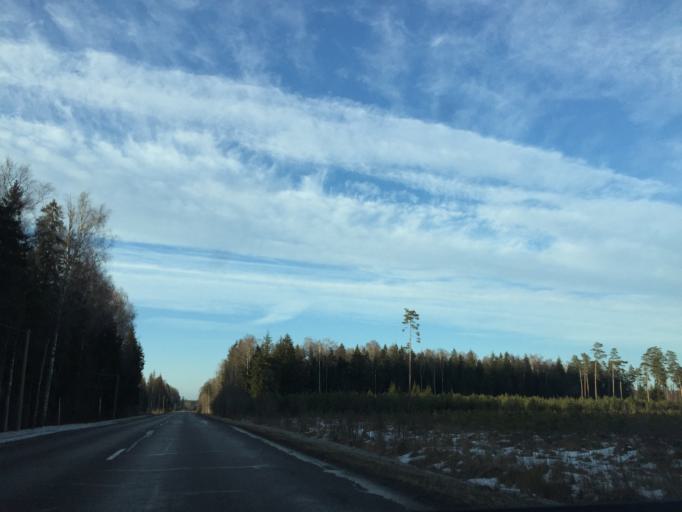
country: LV
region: Kekava
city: Balozi
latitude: 56.8035
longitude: 24.0723
